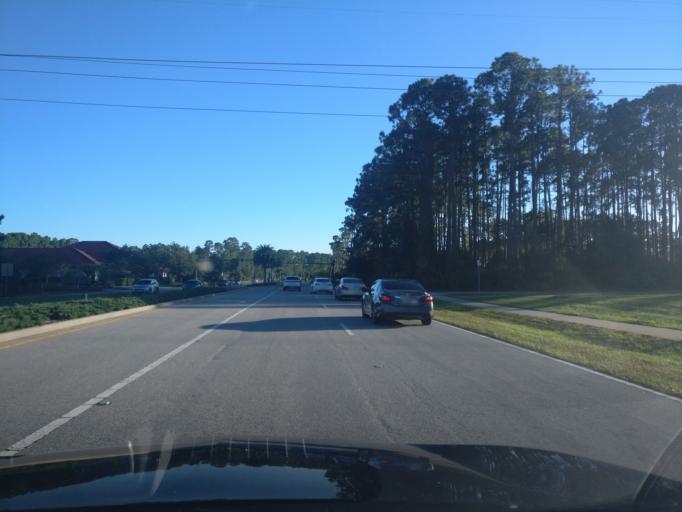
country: US
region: Florida
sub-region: Flagler County
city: Bunnell
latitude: 29.4966
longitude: -81.2198
